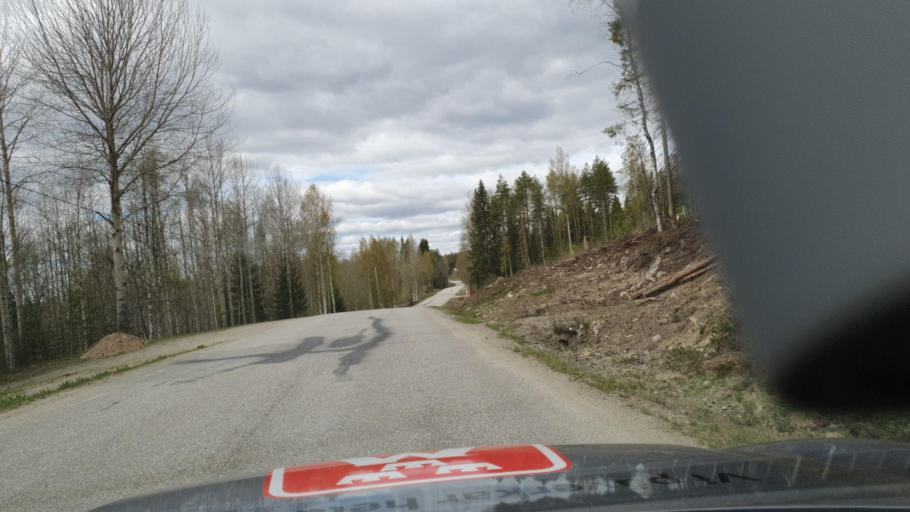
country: SE
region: Vaesternorrland
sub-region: OErnskoeldsviks Kommun
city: Ornskoldsvik
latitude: 63.6385
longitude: 18.7837
